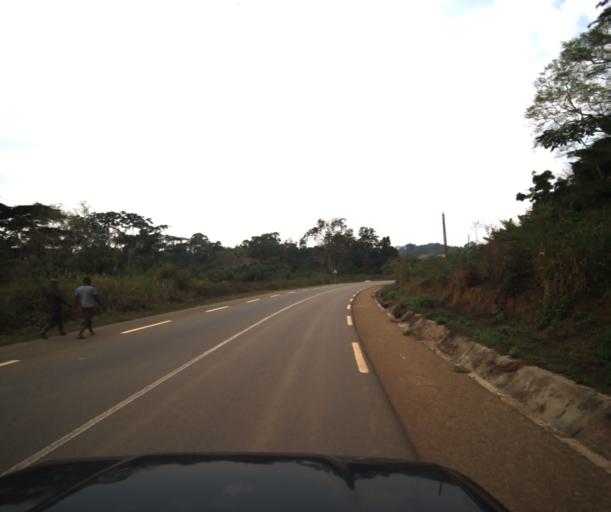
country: CM
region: Centre
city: Akono
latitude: 3.6158
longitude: 11.3137
